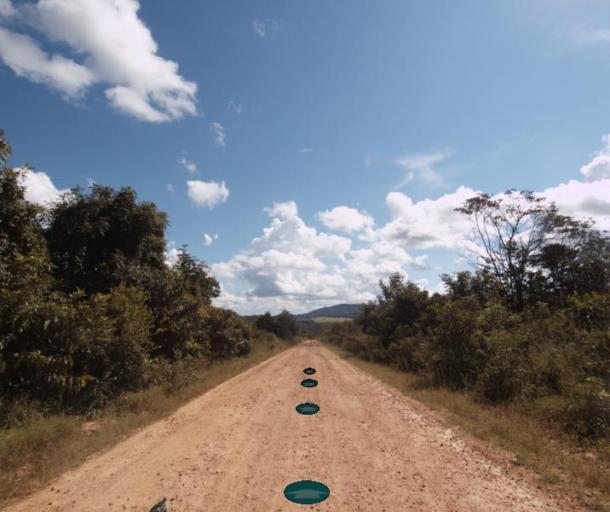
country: BR
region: Goias
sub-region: Pirenopolis
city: Pirenopolis
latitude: -15.7877
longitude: -49.0661
